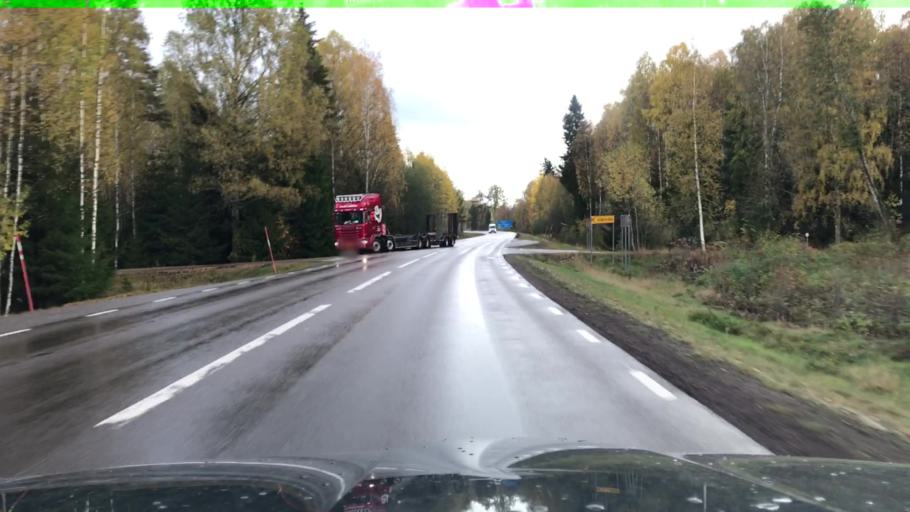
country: SE
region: Vaermland
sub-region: Hagfors Kommun
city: Ekshaerad
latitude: 60.4278
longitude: 13.2490
